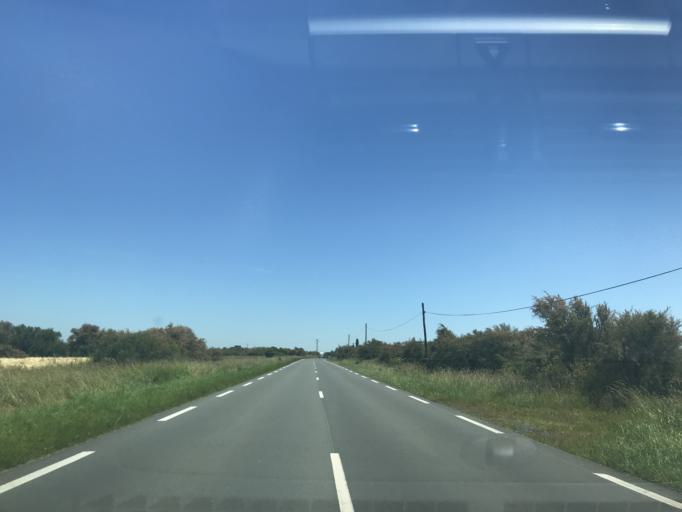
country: FR
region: Poitou-Charentes
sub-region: Departement de la Charente-Maritime
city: Meschers-sur-Gironde
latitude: 45.5600
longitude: -0.9311
